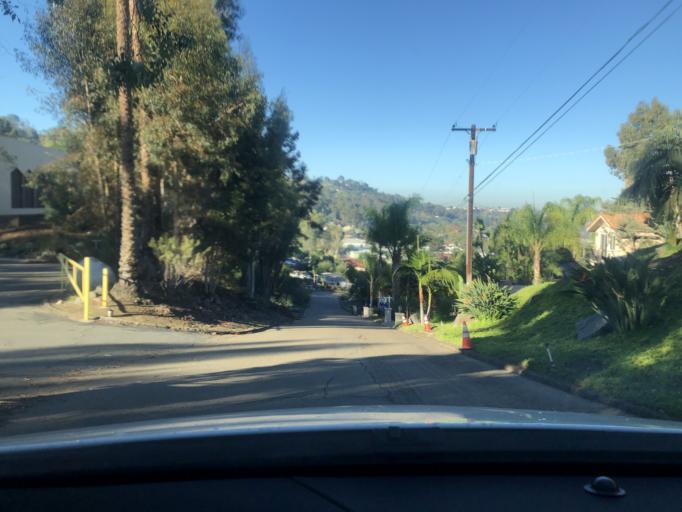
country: US
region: California
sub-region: San Diego County
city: Casa de Oro-Mount Helix
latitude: 32.7755
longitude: -116.9609
